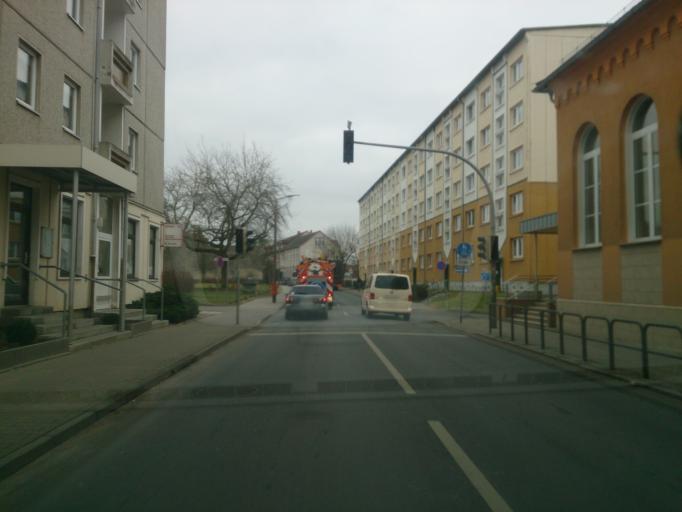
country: DE
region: Mecklenburg-Vorpommern
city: Demmin
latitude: 53.9072
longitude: 13.0316
